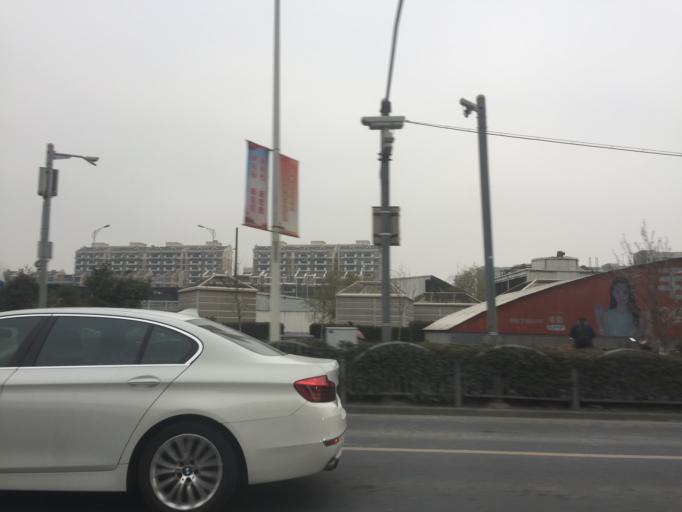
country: CN
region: Shanghai Shi
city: Huamu
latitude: 31.1880
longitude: 121.5060
